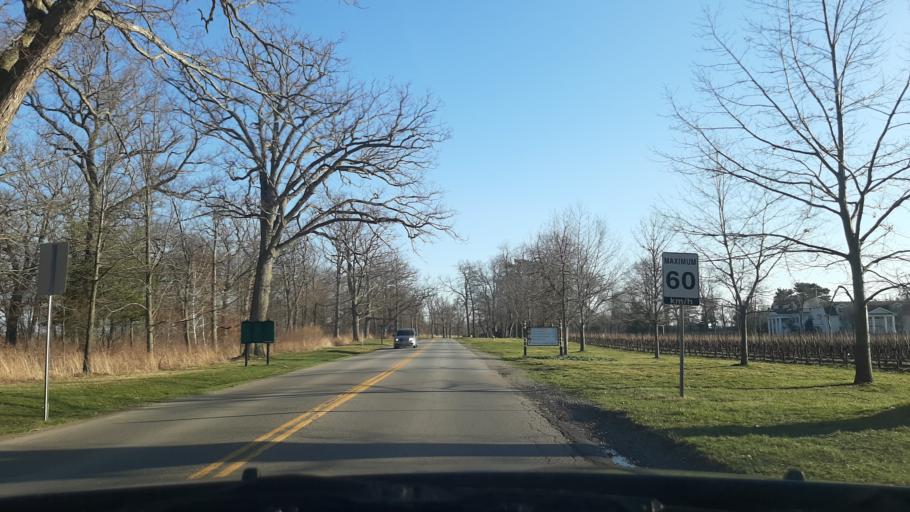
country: US
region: New York
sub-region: Niagara County
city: Youngstown
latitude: 43.2413
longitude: -79.0613
